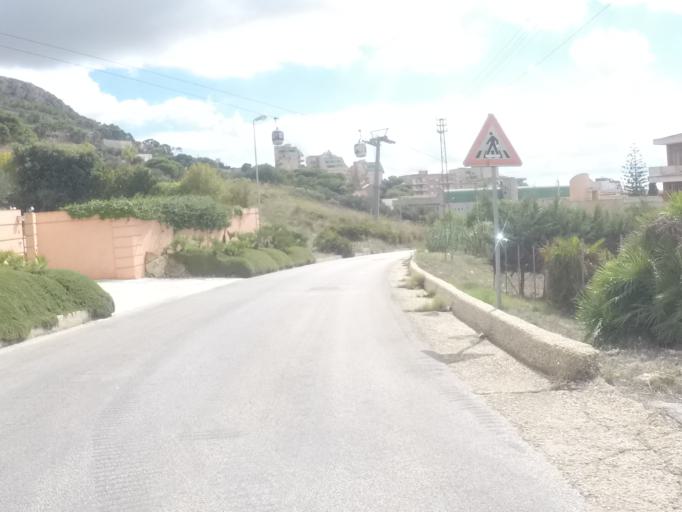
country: IT
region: Sicily
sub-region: Trapani
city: Casa Santa
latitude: 38.0257
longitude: 12.5523
